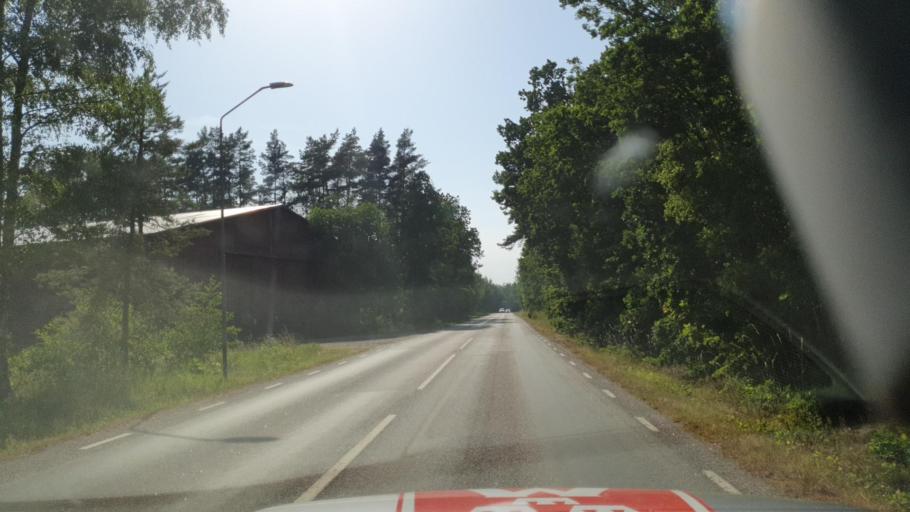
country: SE
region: Kalmar
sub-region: Kalmar Kommun
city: Ljungbyholm
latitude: 56.5912
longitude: 16.1596
